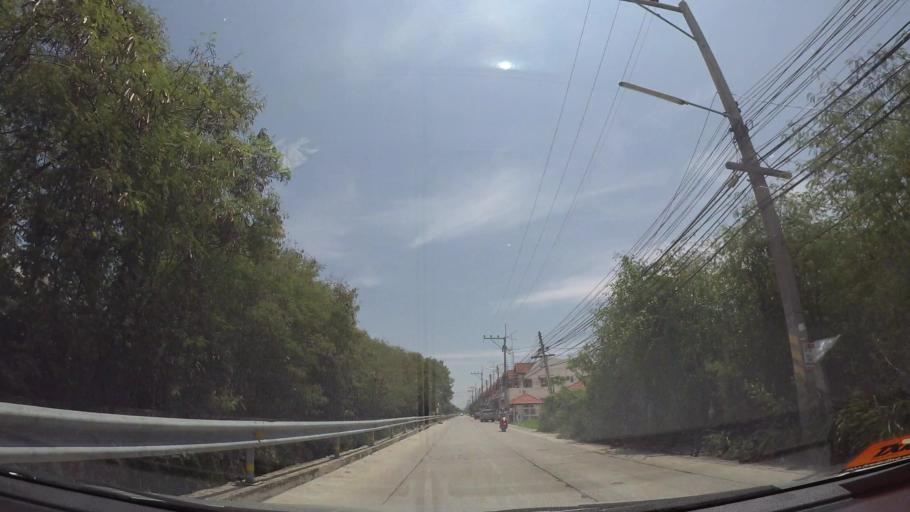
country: TH
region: Chon Buri
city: Chon Buri
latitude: 13.3246
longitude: 100.9435
